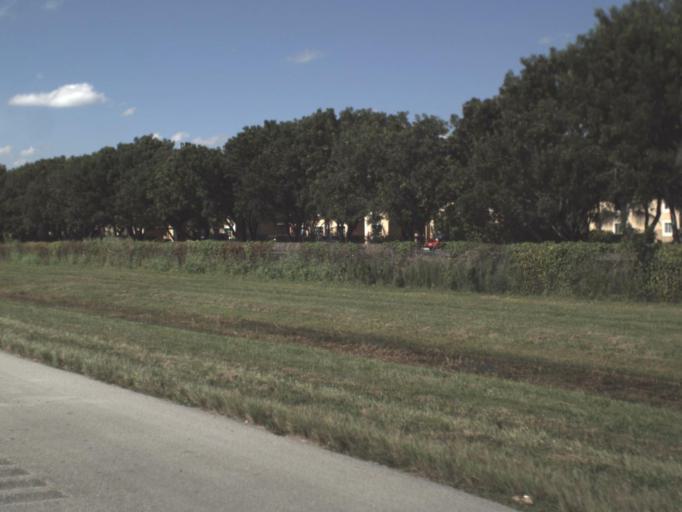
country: US
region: Florida
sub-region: Miami-Dade County
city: Homestead
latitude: 25.4656
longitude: -80.4580
